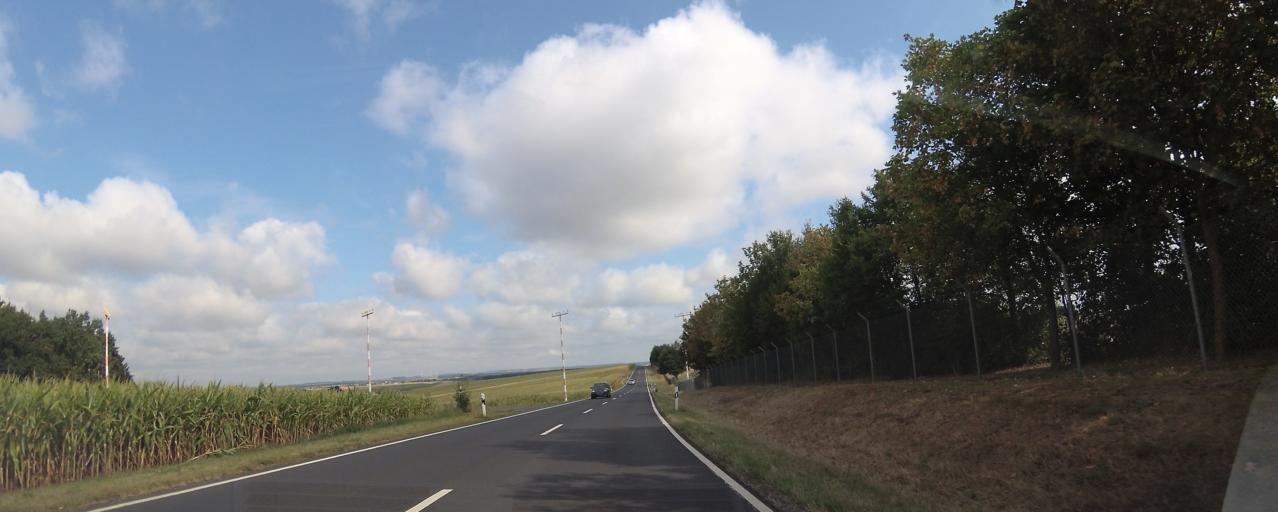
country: DE
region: Rheinland-Pfalz
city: Beilingen
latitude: 49.9616
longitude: 6.6770
